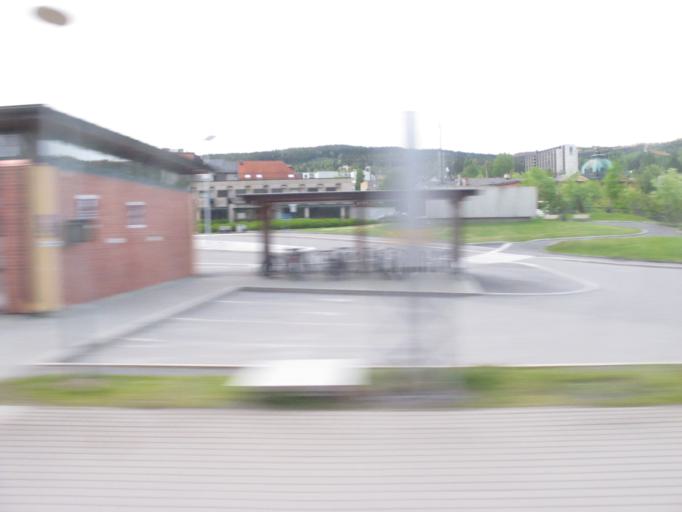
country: NO
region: Oppland
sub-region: Lillehammer
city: Lillehammer
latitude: 61.1141
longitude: 10.4613
